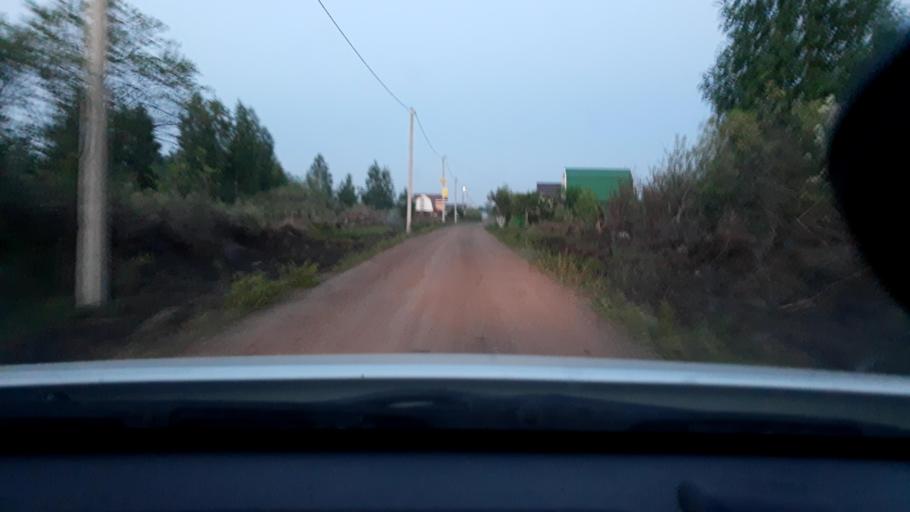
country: RU
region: Bashkortostan
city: Avdon
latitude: 54.5292
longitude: 55.8148
